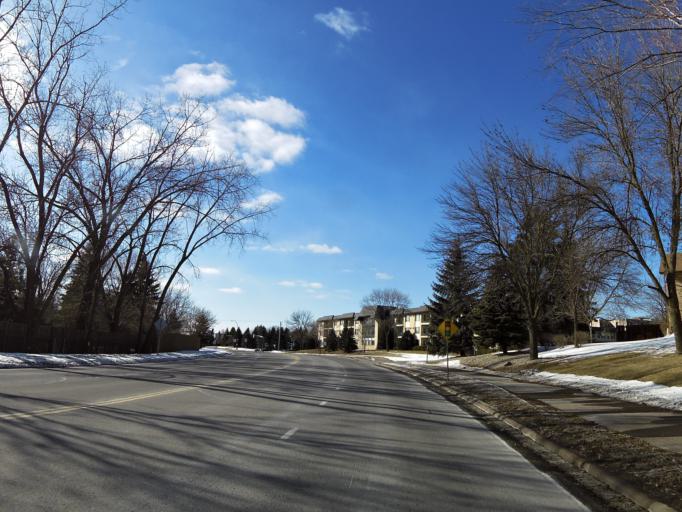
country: US
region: Minnesota
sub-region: Washington County
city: Woodbury
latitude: 44.9064
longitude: -92.9621
